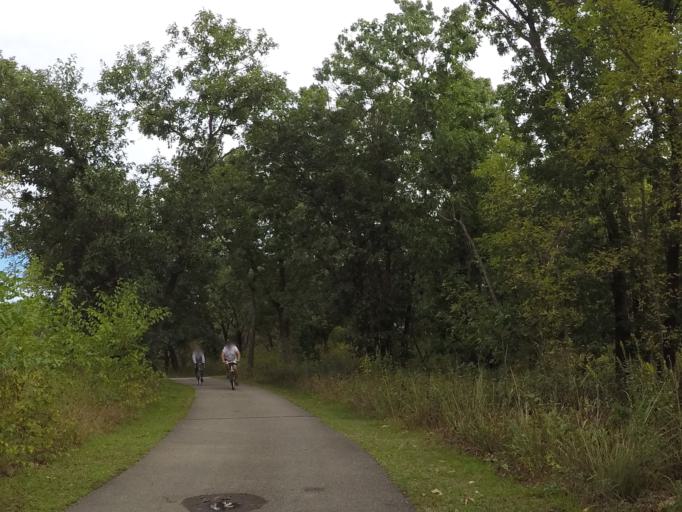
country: US
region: Wisconsin
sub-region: Sauk County
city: Sauk City
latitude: 43.2760
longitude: -89.7184
